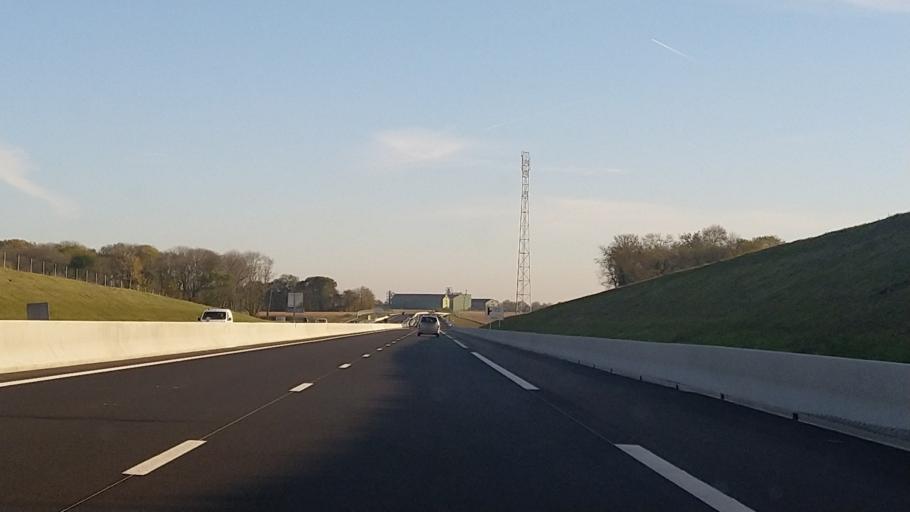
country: FR
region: Ile-de-France
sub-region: Departement du Val-d'Oise
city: Maffliers
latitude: 49.0859
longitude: 2.3170
